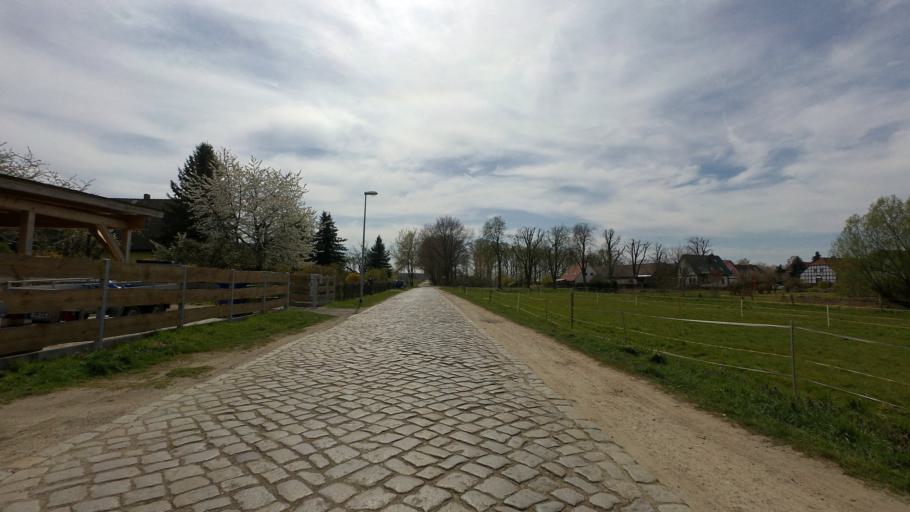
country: DE
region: Brandenburg
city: Schulzendorf
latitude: 52.3369
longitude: 13.5437
